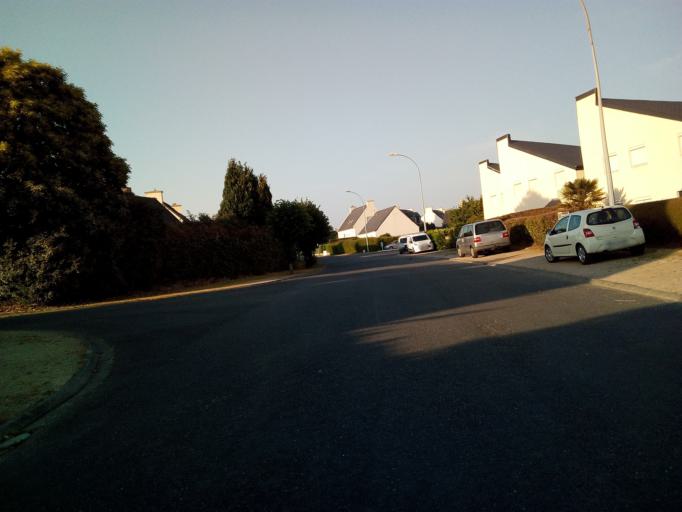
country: FR
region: Brittany
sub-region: Departement du Finistere
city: Landivisiau
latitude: 48.4974
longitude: -4.0821
